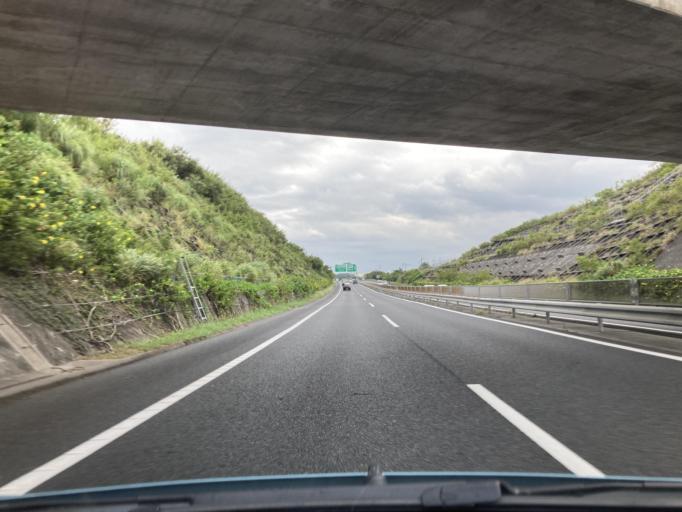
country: JP
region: Okinawa
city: Ginowan
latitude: 26.2347
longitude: 127.7402
